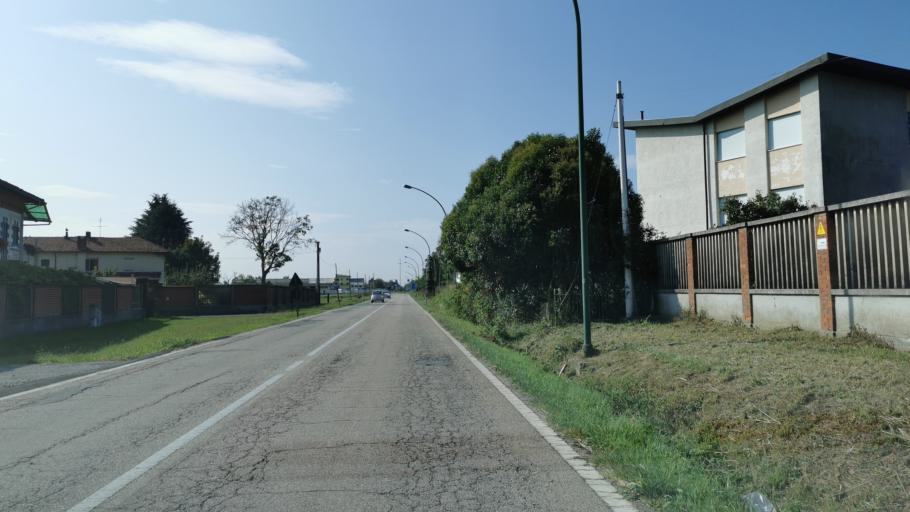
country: IT
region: Piedmont
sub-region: Provincia di Torino
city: Leini
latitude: 45.2053
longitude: 7.7274
